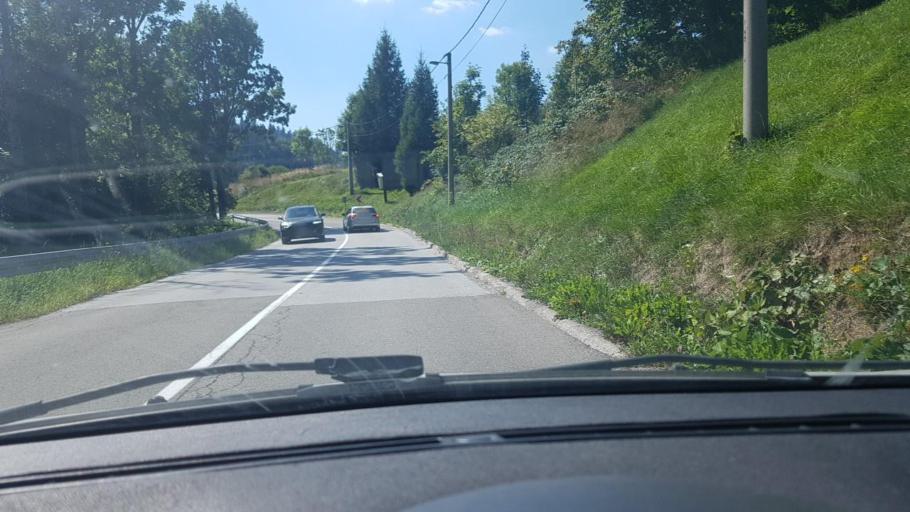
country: HR
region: Primorsko-Goranska
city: Vrbovsko
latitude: 45.3773
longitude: 14.9619
